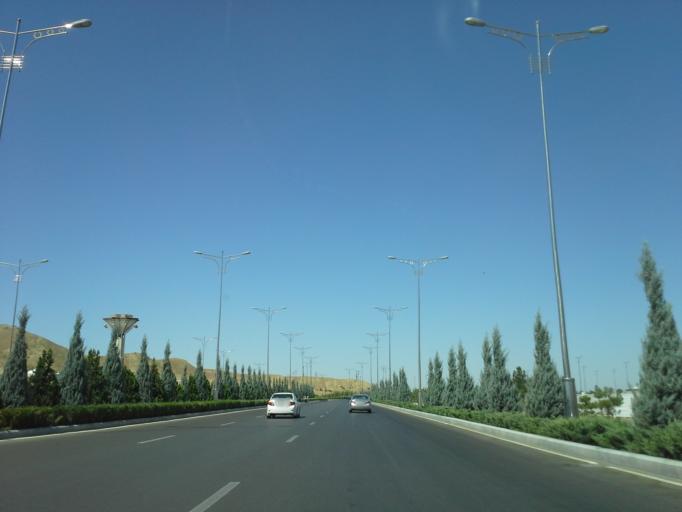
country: TM
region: Ahal
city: Ashgabat
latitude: 37.9338
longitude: 58.3202
